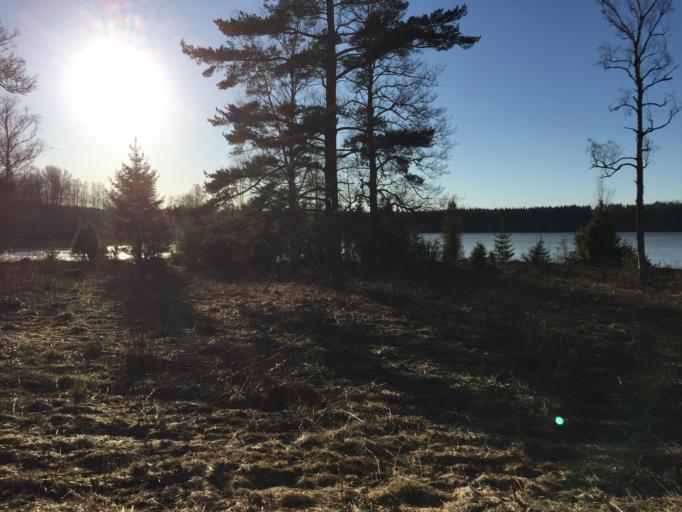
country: SE
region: Soedermanland
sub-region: Vingakers Kommun
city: Vingaker
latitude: 59.0008
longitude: 15.6758
